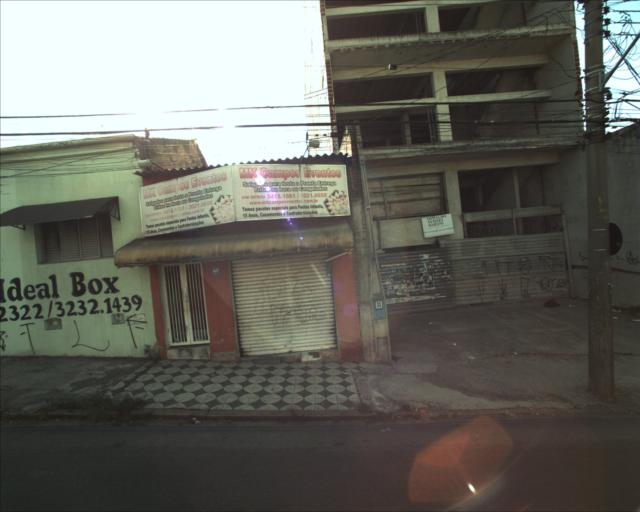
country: BR
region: Sao Paulo
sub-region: Sorocaba
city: Sorocaba
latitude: -23.4934
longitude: -47.4580
